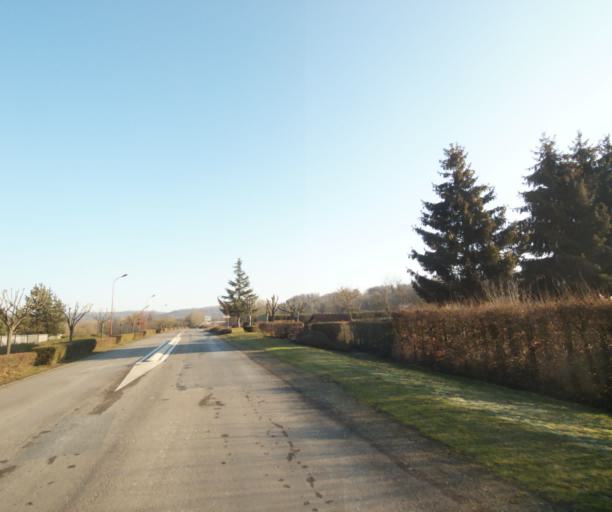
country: FR
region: Champagne-Ardenne
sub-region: Departement de la Haute-Marne
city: Chevillon
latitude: 48.5440
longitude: 5.0908
